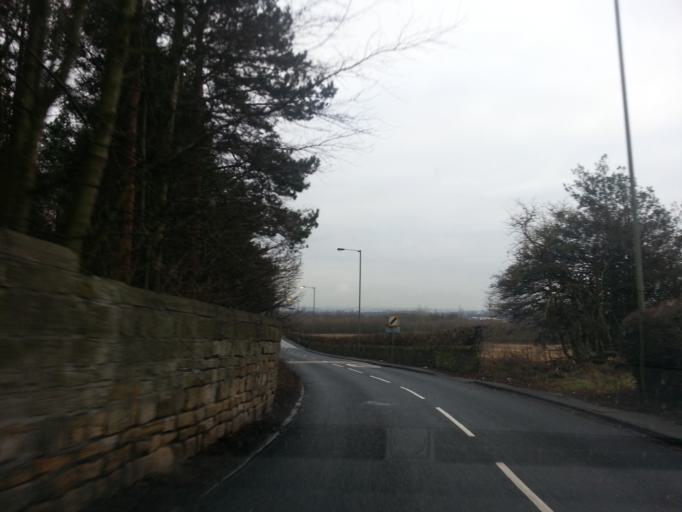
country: GB
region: England
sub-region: County Durham
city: Chester-le-Street
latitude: 54.8709
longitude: -1.5638
